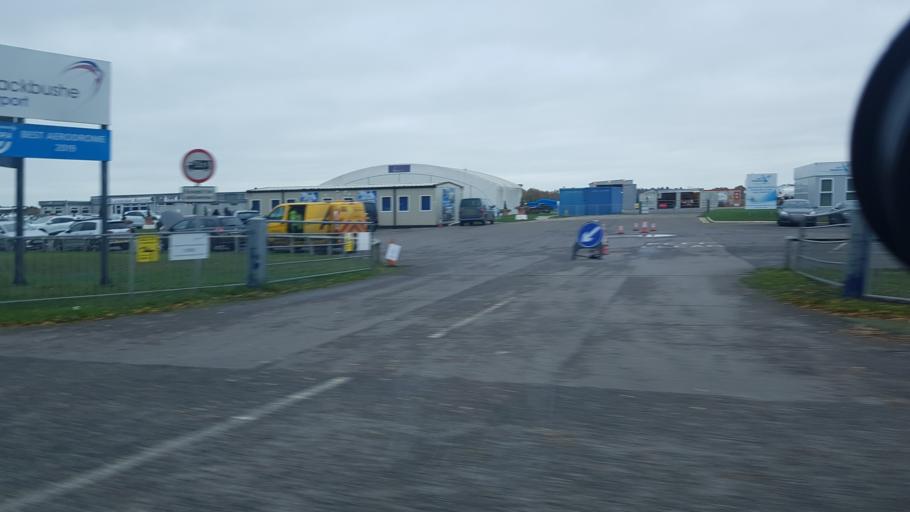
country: GB
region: England
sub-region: Hampshire
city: Yateley
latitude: 51.3222
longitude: -0.8403
